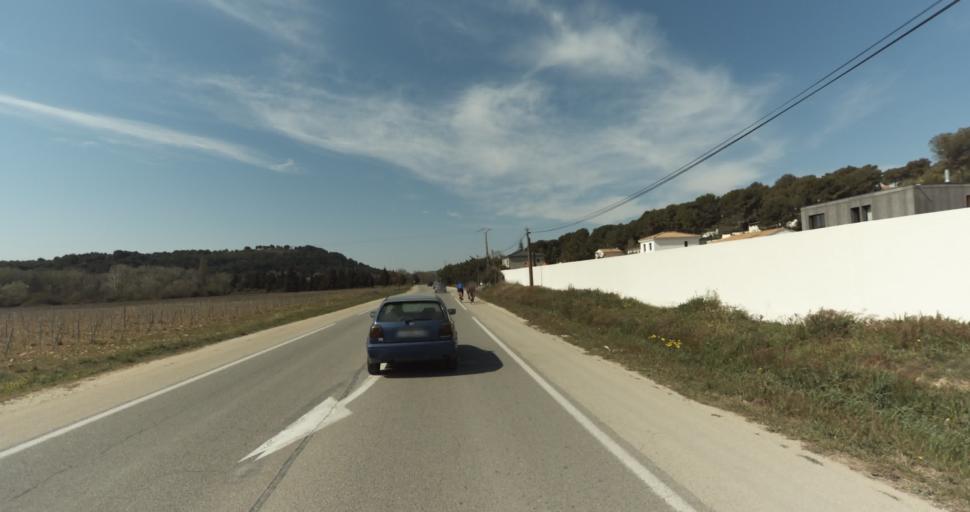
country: FR
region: Provence-Alpes-Cote d'Azur
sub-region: Departement des Bouches-du-Rhone
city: Velaux
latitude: 43.5407
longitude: 5.2647
